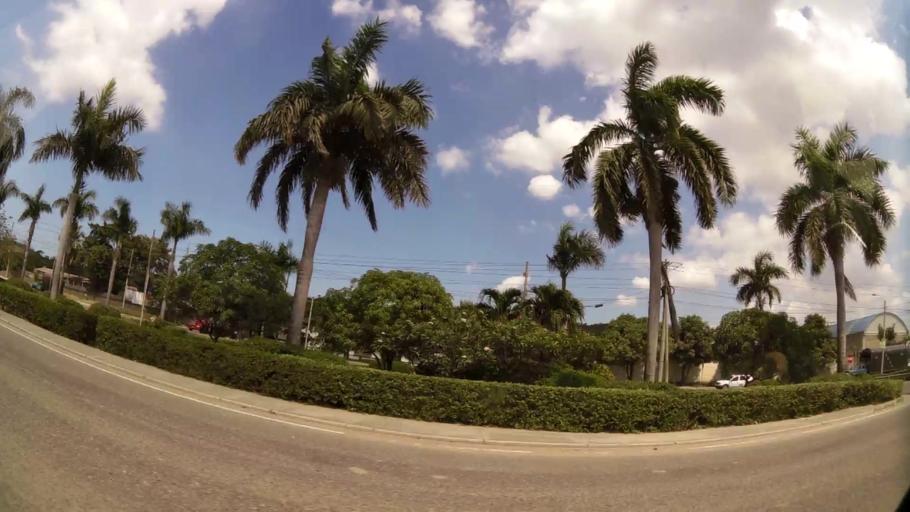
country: CO
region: Bolivar
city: Cartagena
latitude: 10.3544
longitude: -75.4975
